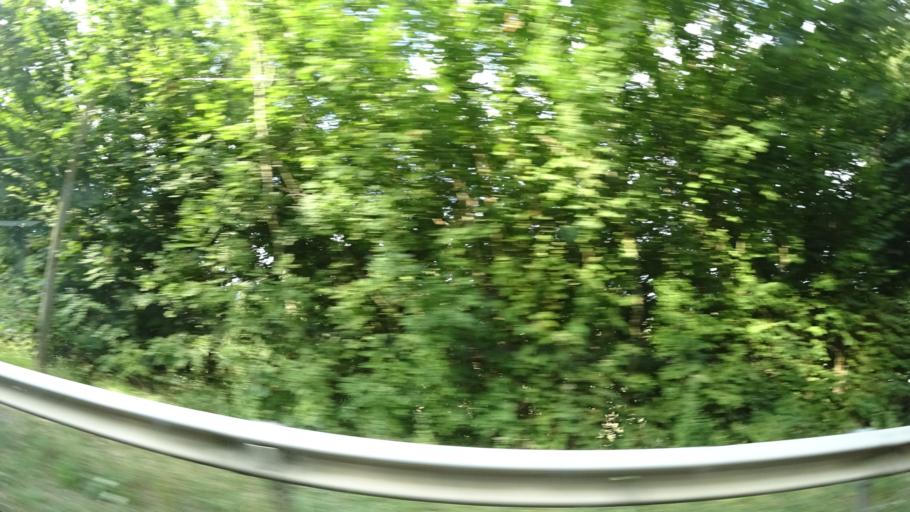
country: FR
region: Midi-Pyrenees
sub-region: Departement de l'Aveyron
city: Saint-Christophe-Vallon
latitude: 44.4998
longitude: 2.3734
